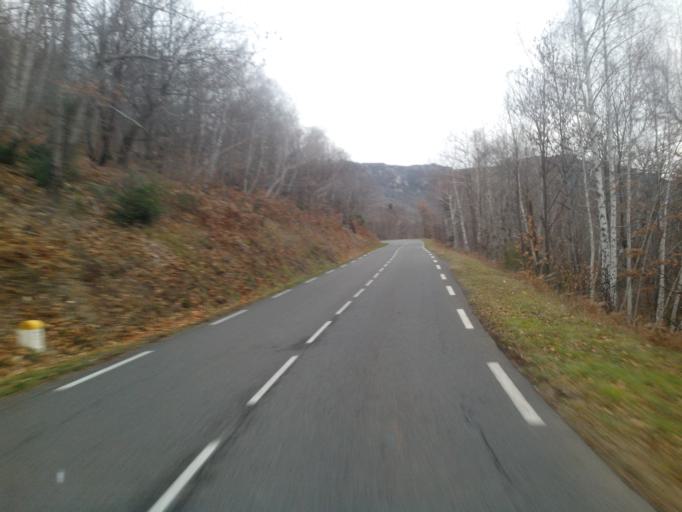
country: FR
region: Languedoc-Roussillon
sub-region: Departement de la Lozere
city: Florac
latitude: 44.2779
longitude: 3.5984
